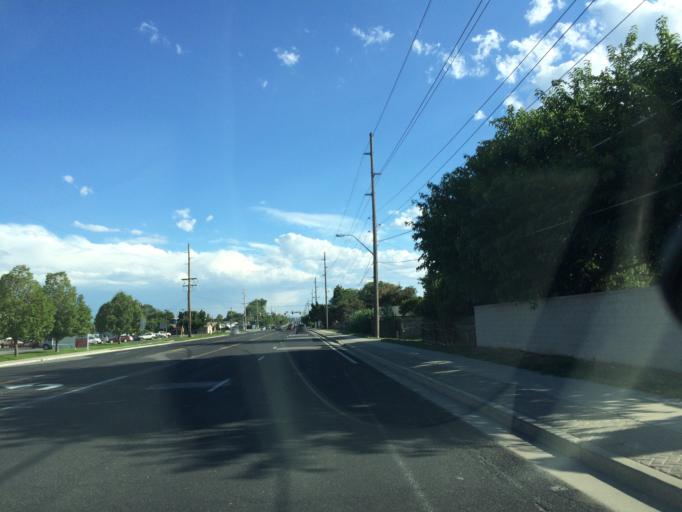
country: US
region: Utah
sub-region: Salt Lake County
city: Taylorsville
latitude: 40.6915
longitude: -111.9580
